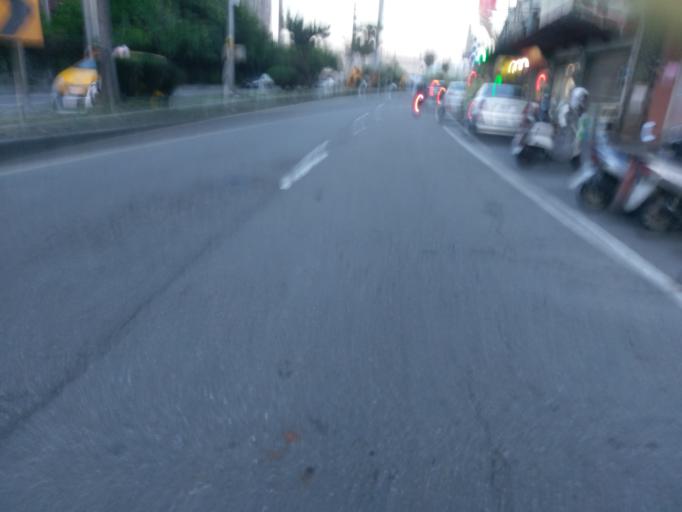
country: TW
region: Taiwan
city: Taoyuan City
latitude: 25.0544
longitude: 121.1219
